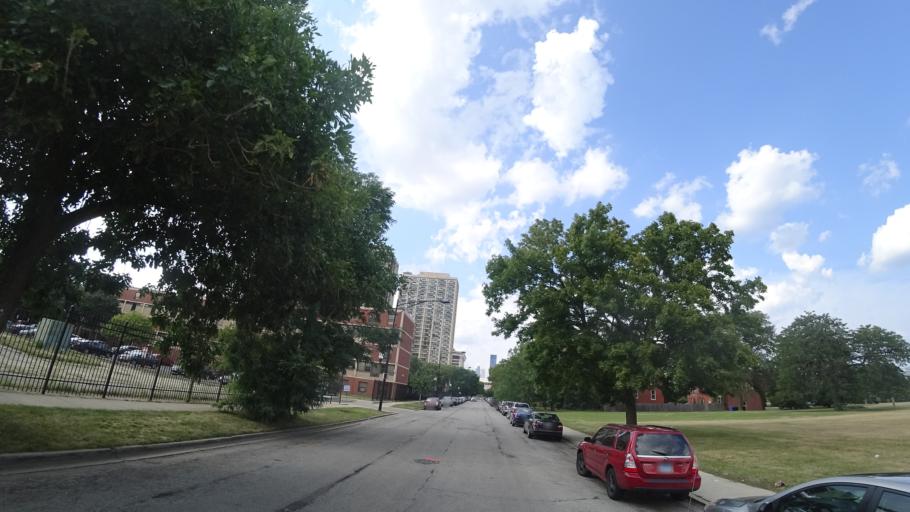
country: US
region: Illinois
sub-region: Cook County
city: Chicago
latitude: 41.8424
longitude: -87.6204
